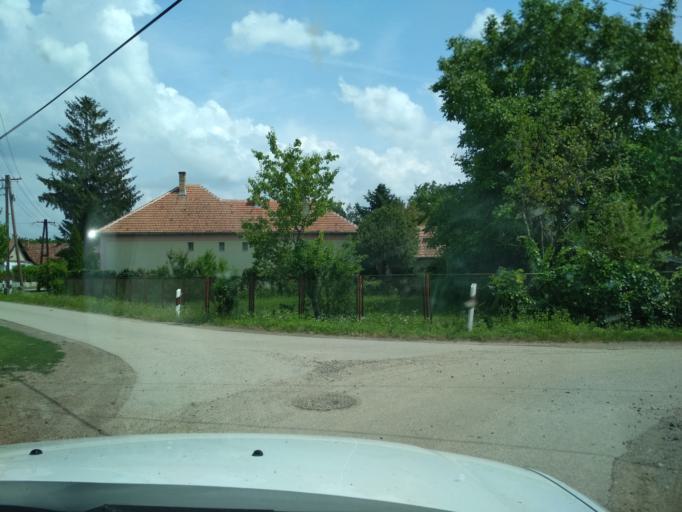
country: HU
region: Pest
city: Tapioszentmarton
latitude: 47.3430
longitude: 19.7378
